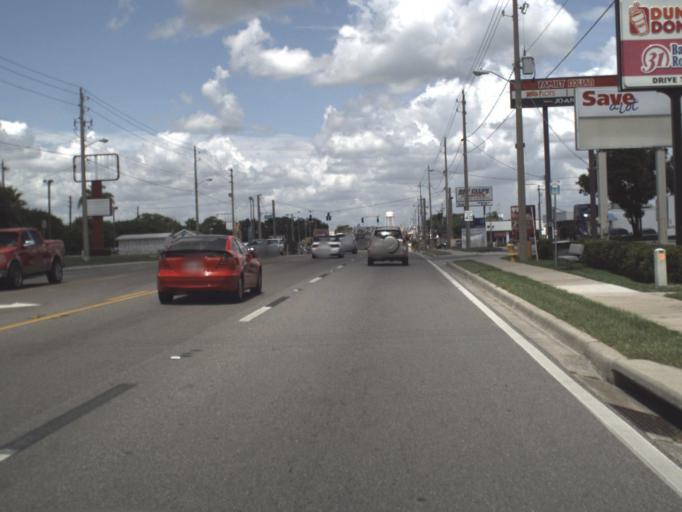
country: US
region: Florida
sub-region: Polk County
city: Winter Haven
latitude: 28.0061
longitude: -81.7308
